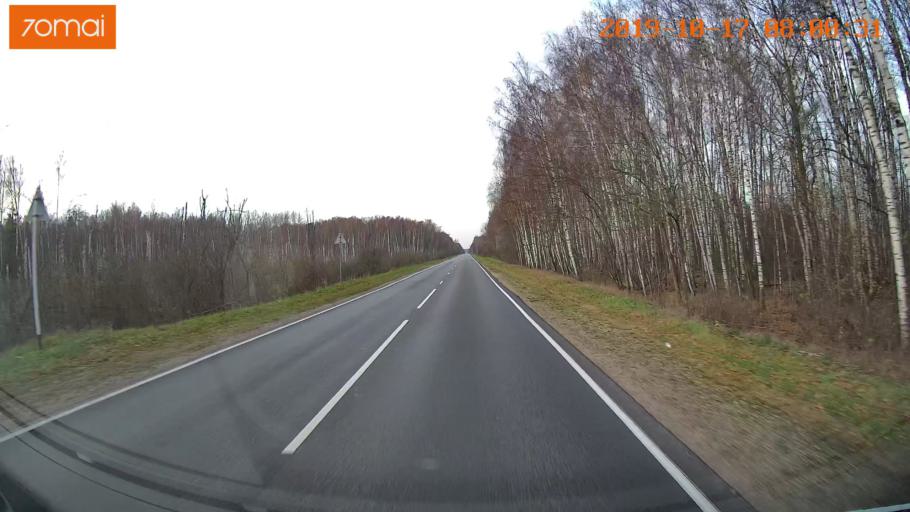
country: RU
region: Vladimir
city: Bavleny
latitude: 56.3825
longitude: 39.5162
